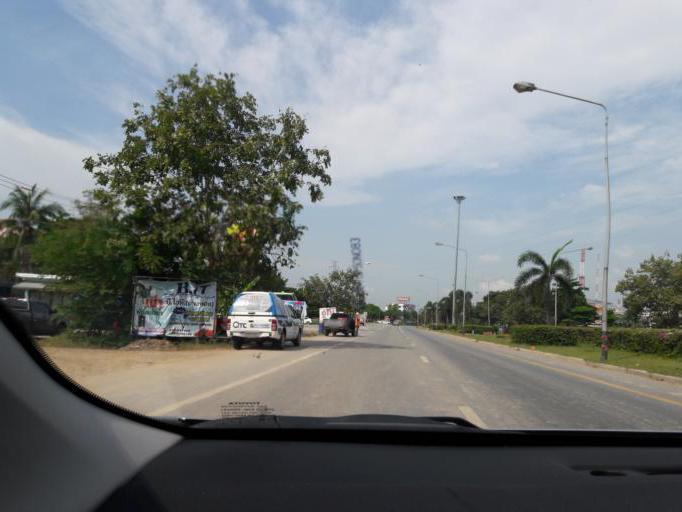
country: TH
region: Ang Thong
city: Ang Thong
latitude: 14.5816
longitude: 100.4605
